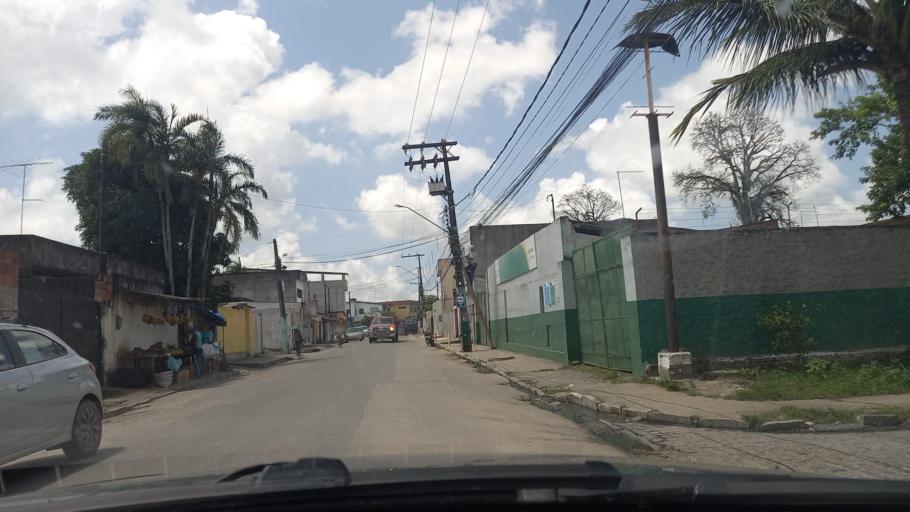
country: BR
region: Pernambuco
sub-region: Goiana
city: Goiana
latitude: -7.5635
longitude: -35.0069
